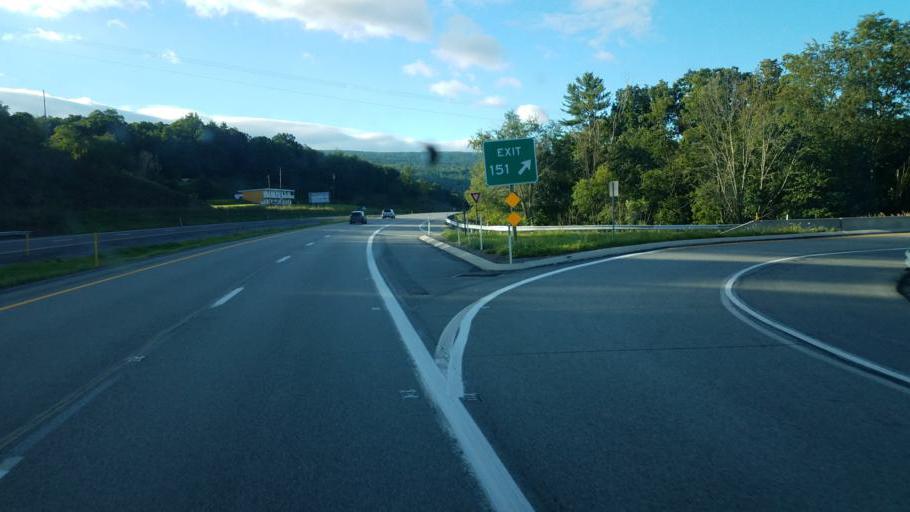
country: US
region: Pennsylvania
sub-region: Bedford County
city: Earlston
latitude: 39.9477
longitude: -78.2297
